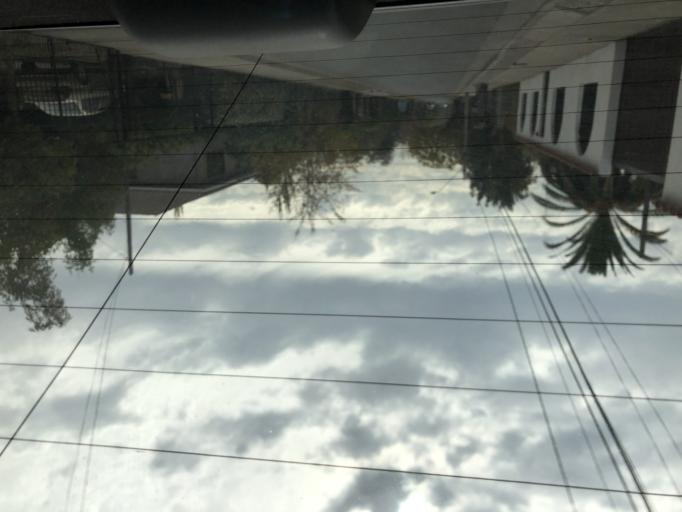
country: CL
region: Santiago Metropolitan
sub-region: Provincia de Cordillera
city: Puente Alto
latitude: -33.6115
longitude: -70.5343
